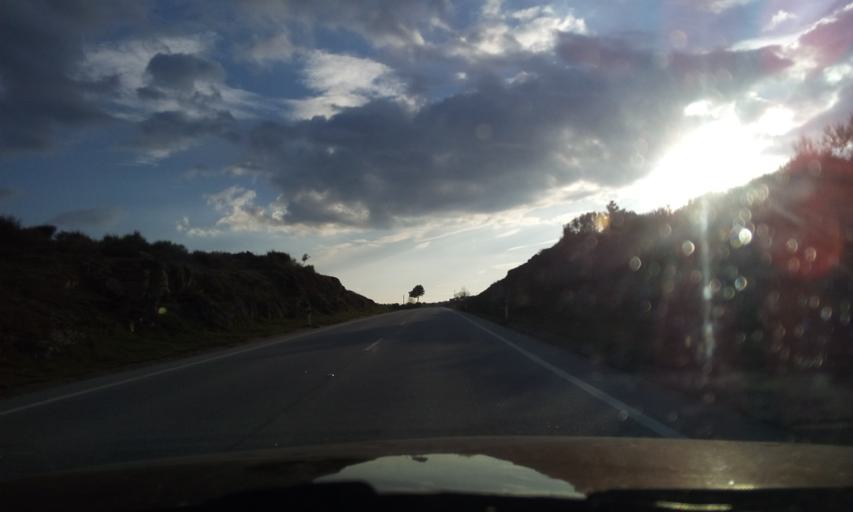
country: PT
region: Guarda
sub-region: Pinhel
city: Pinhel
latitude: 40.6682
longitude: -6.9566
